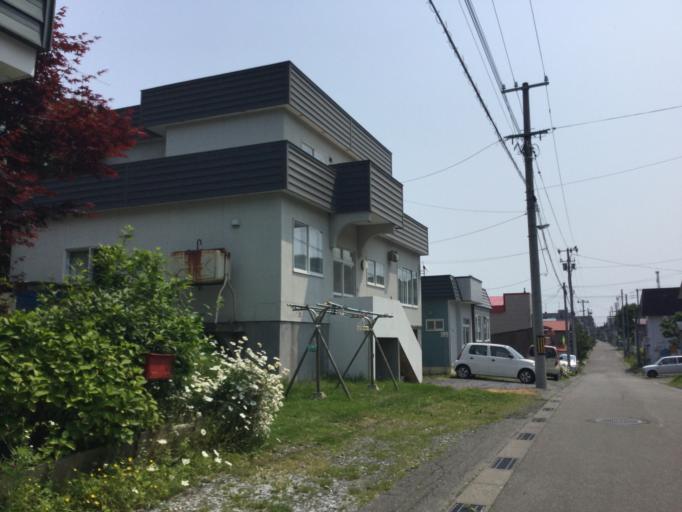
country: JP
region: Hokkaido
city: Wakkanai
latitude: 45.4017
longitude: 141.6752
